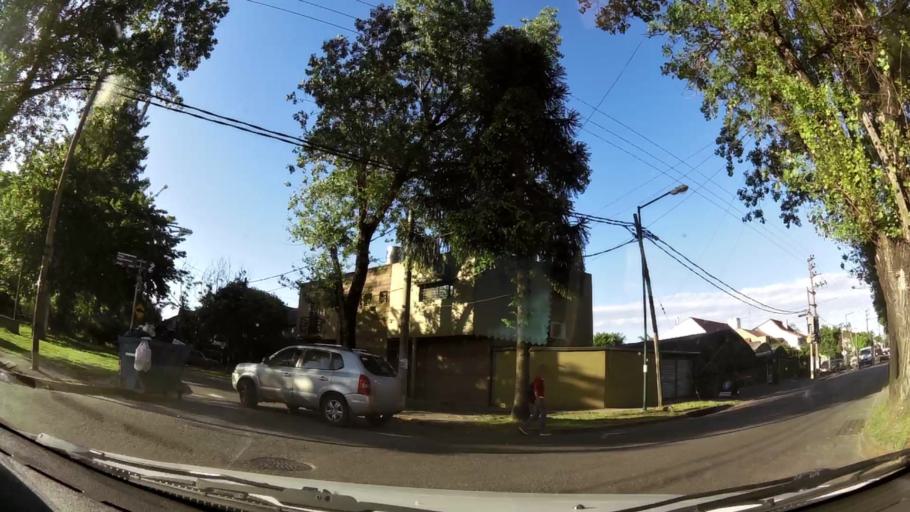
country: AR
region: Buenos Aires
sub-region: Partido de San Isidro
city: San Isidro
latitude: -34.4729
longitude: -58.5514
